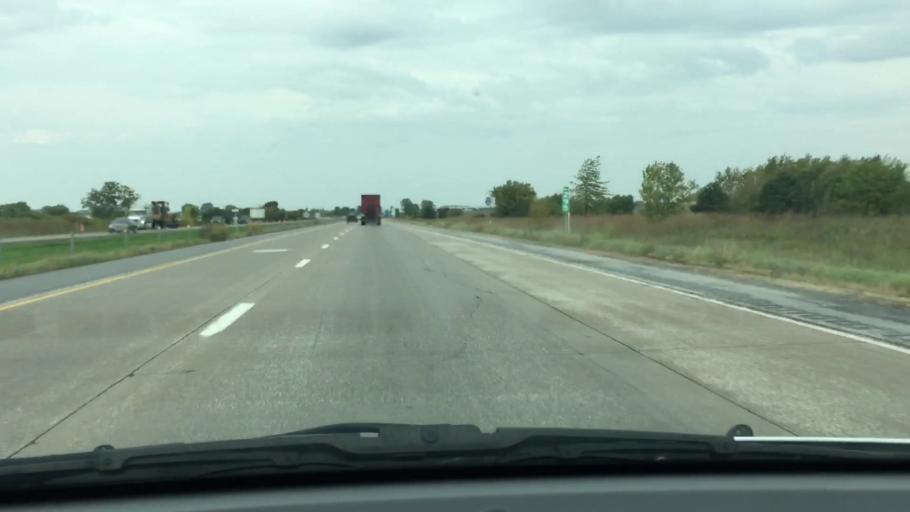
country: US
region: Iowa
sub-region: Scott County
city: Eldridge
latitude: 41.5981
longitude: -90.5798
